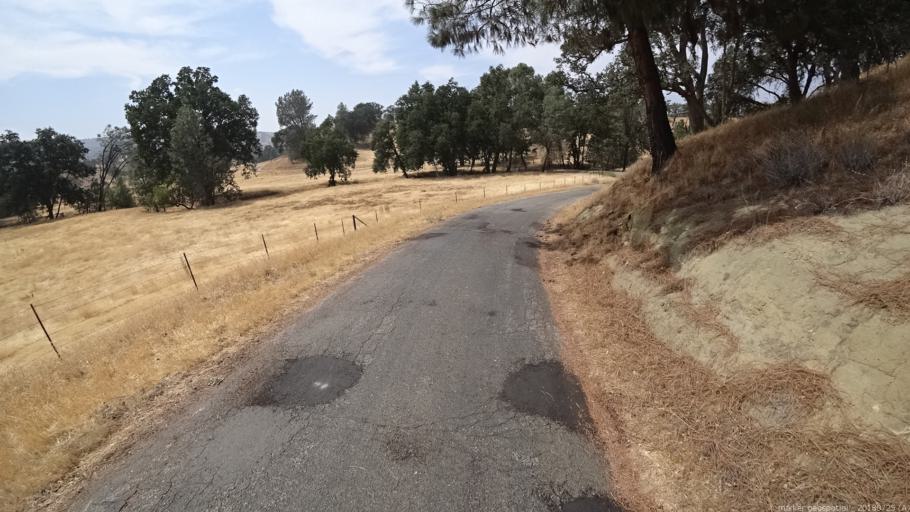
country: US
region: California
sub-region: Fresno County
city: Coalinga
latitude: 36.1829
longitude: -120.6826
